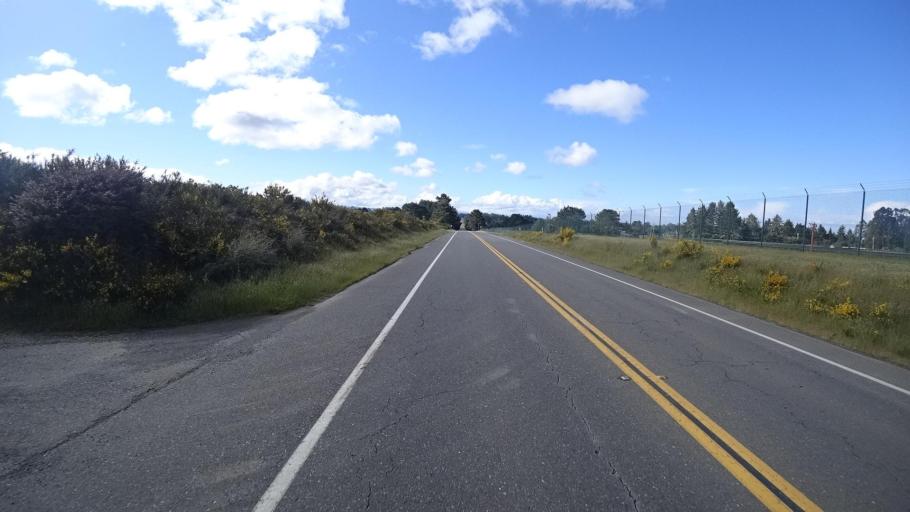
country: US
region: California
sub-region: Humboldt County
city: McKinleyville
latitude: 40.9678
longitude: -124.1007
